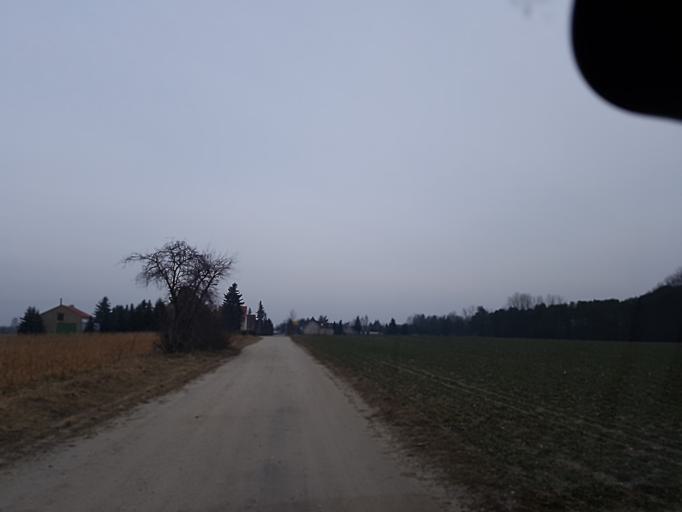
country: DE
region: Brandenburg
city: Ruckersdorf
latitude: 51.5881
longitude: 13.5436
